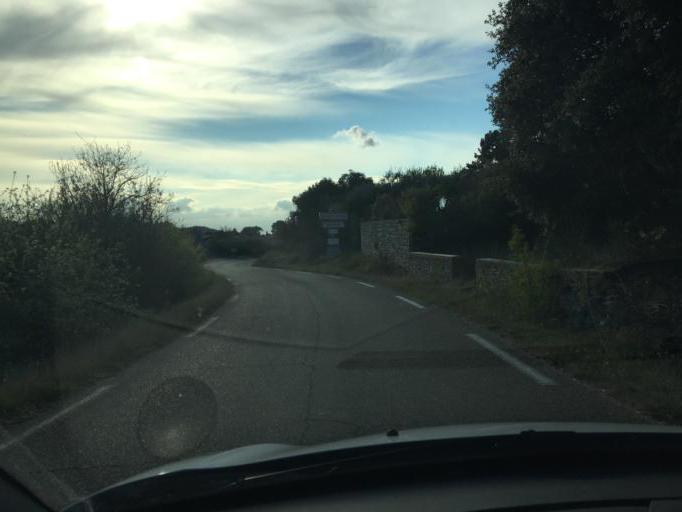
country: FR
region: Provence-Alpes-Cote d'Azur
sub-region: Departement du Vaucluse
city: Villes-sur-Auzon
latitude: 44.0538
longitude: 5.2395
